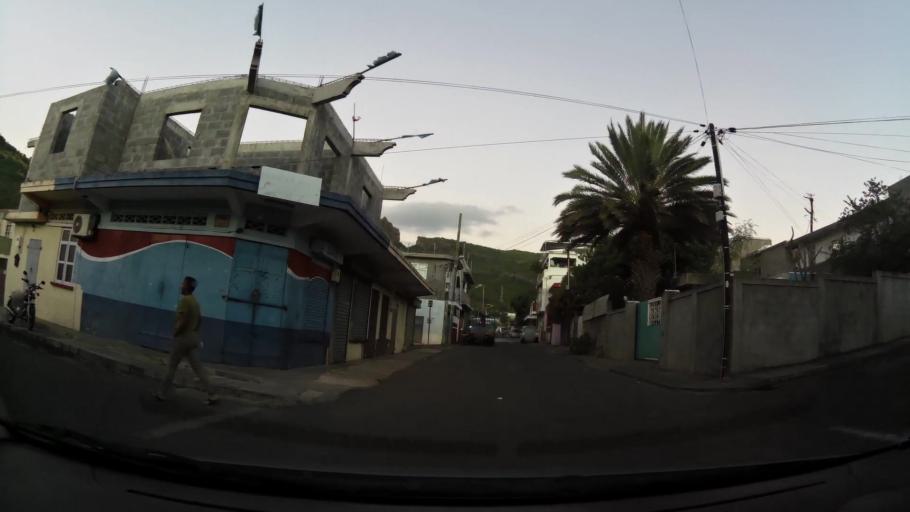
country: MU
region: Port Louis
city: Port Louis
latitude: -20.1687
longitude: 57.5173
